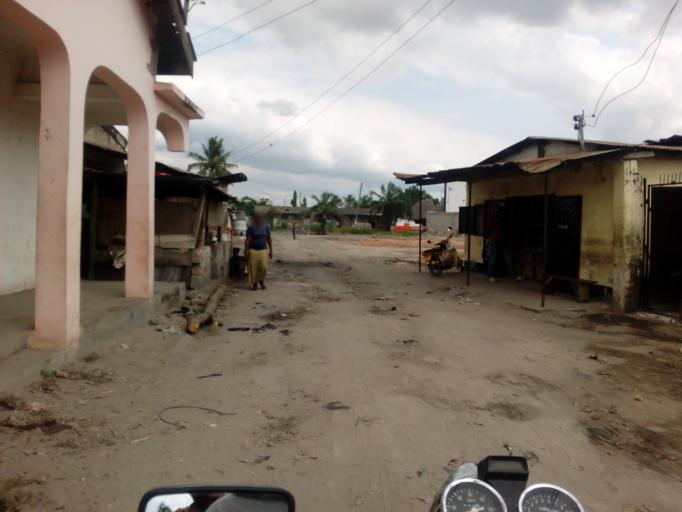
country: TZ
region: Dar es Salaam
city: Dar es Salaam
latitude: -6.8485
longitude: 39.2582
